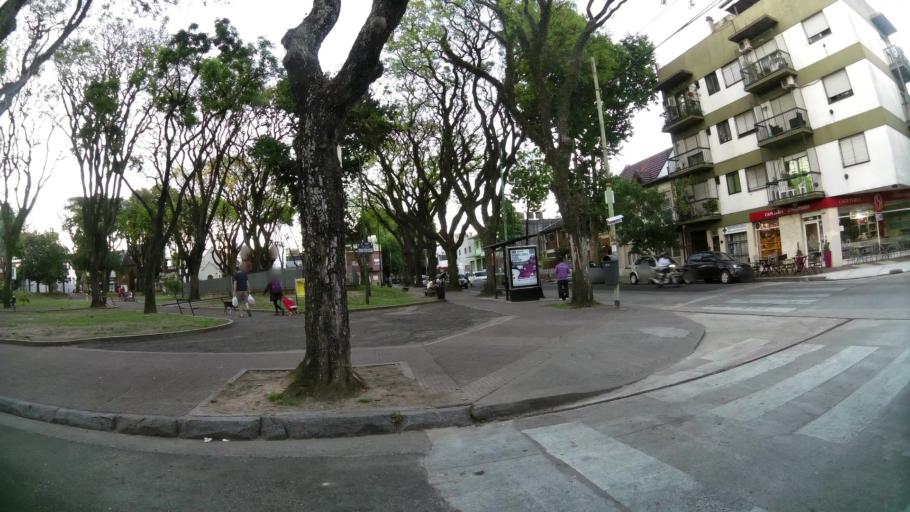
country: AR
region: Buenos Aires
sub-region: Partido de Vicente Lopez
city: Olivos
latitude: -34.5443
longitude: -58.4768
